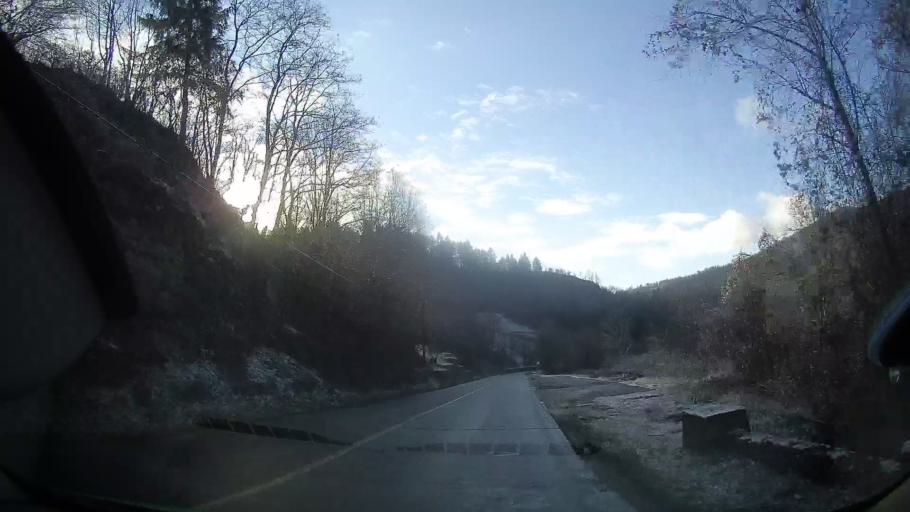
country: RO
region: Alba
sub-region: Comuna Sohodol
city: Sohodol
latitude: 46.3662
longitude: 23.0293
